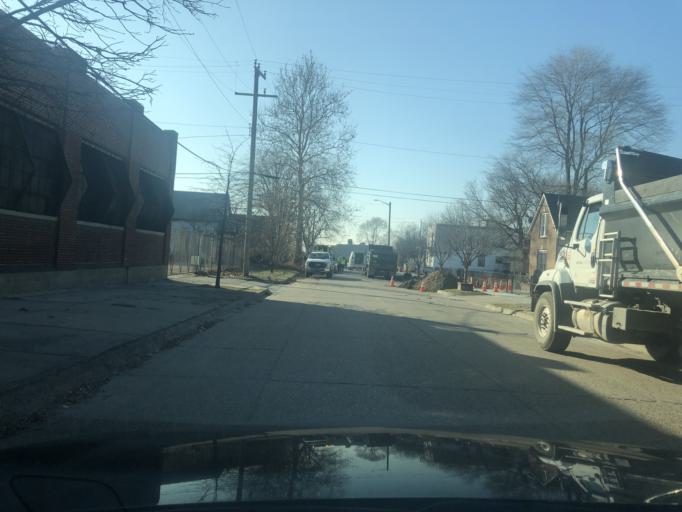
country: US
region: Michigan
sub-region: Wayne County
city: River Rouge
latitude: 42.3061
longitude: -83.0937
